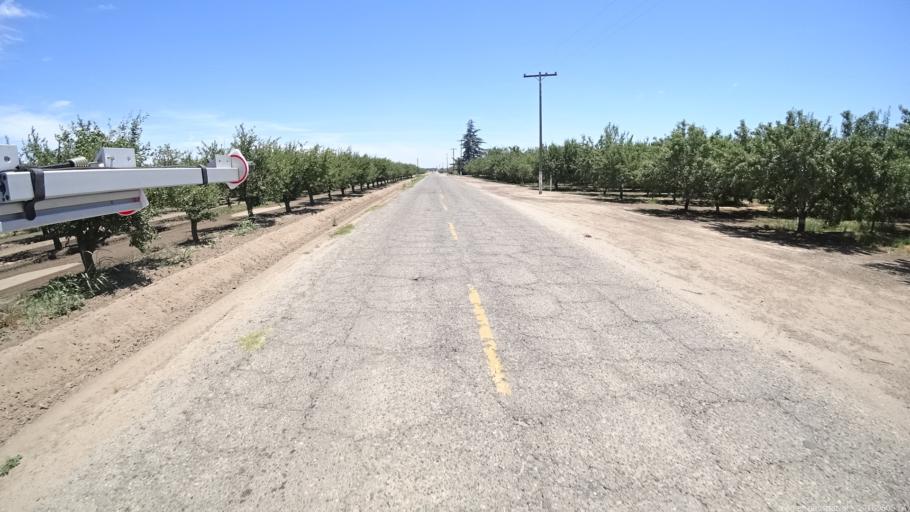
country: US
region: California
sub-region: Madera County
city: Chowchilla
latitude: 37.1200
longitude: -120.3015
